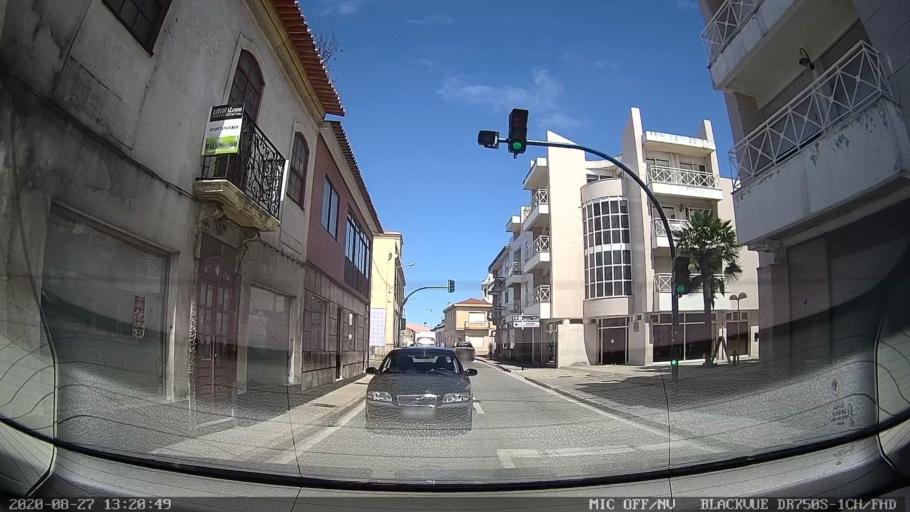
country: PT
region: Aveiro
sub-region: Vagos
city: Vagos
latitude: 40.5550
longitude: -8.6815
